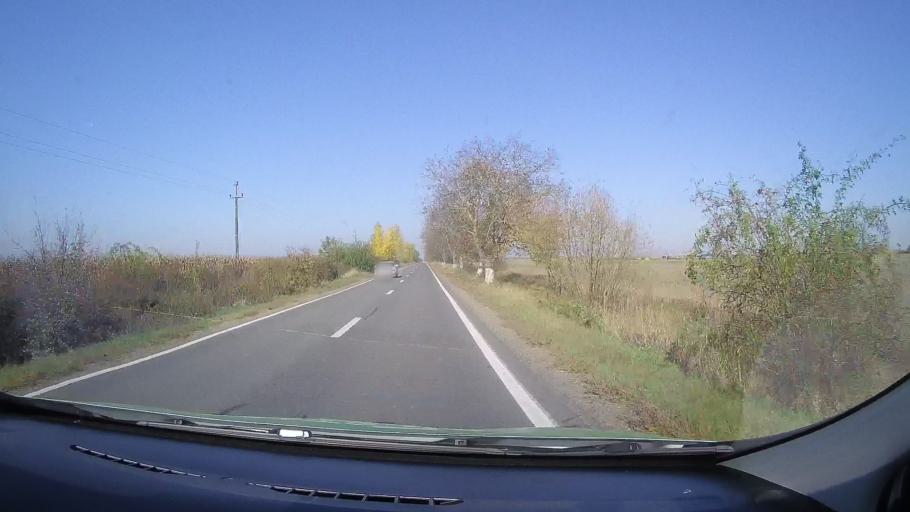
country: RO
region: Satu Mare
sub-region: Comuna Urziceni
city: Urziceni
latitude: 47.7150
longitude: 22.4226
